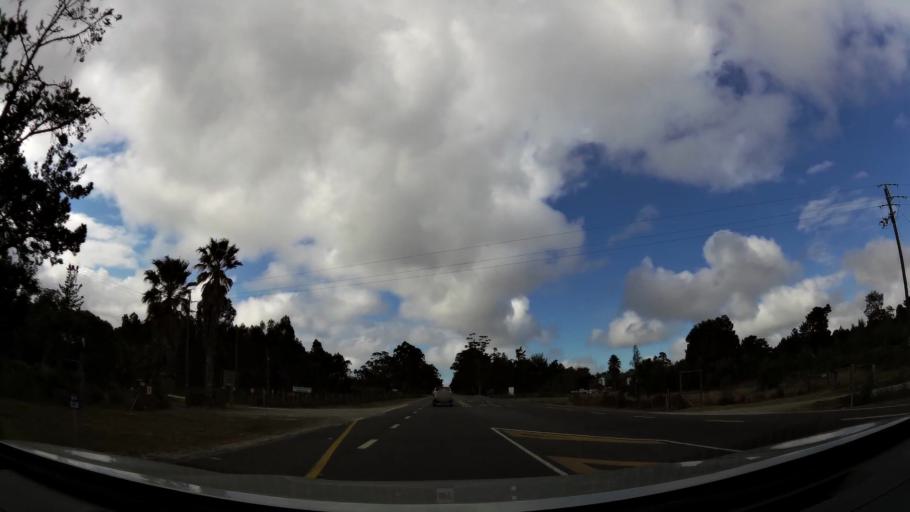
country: ZA
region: Western Cape
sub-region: Eden District Municipality
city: Plettenberg Bay
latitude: -34.0443
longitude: 23.2842
